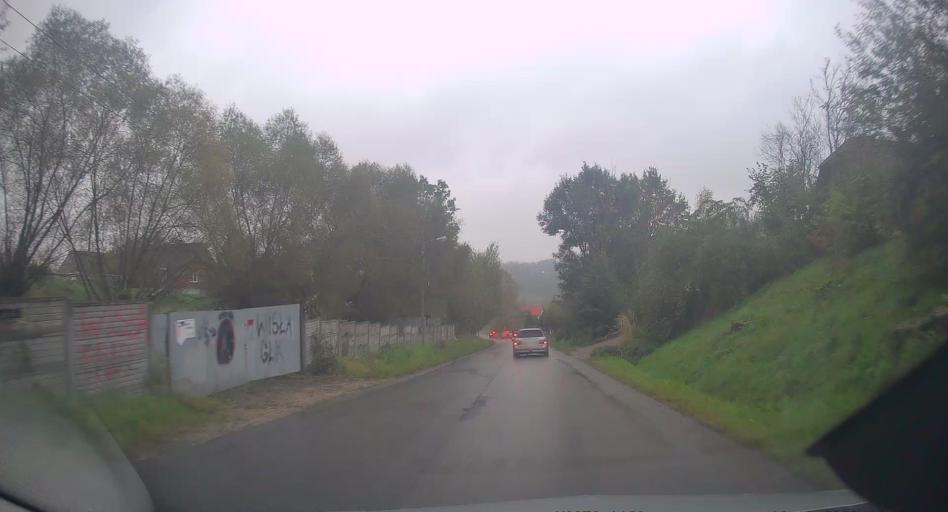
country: PL
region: Lesser Poland Voivodeship
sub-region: Powiat krakowski
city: Ochojno
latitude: 49.9689
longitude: 19.9981
